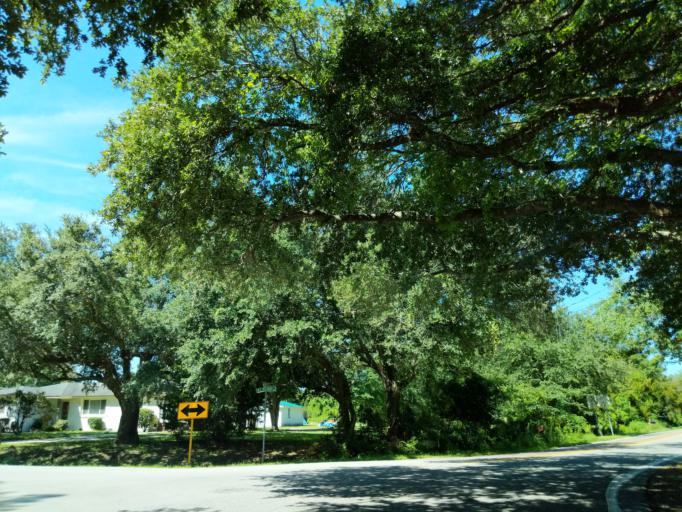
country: US
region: South Carolina
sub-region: Charleston County
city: Folly Beach
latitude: 32.7027
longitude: -79.9588
